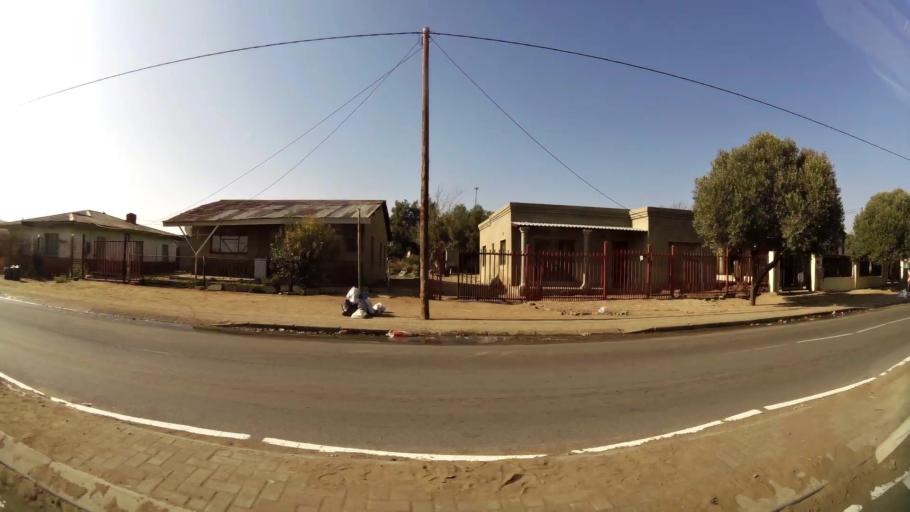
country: ZA
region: Orange Free State
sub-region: Mangaung Metropolitan Municipality
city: Bloemfontein
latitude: -29.1578
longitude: 26.2410
